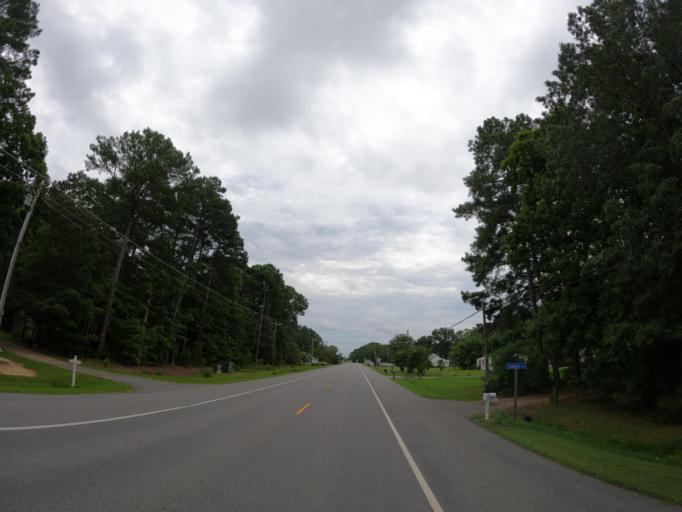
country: US
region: Maryland
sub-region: Saint Mary's County
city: Lexington Park
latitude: 38.1493
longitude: -76.5132
